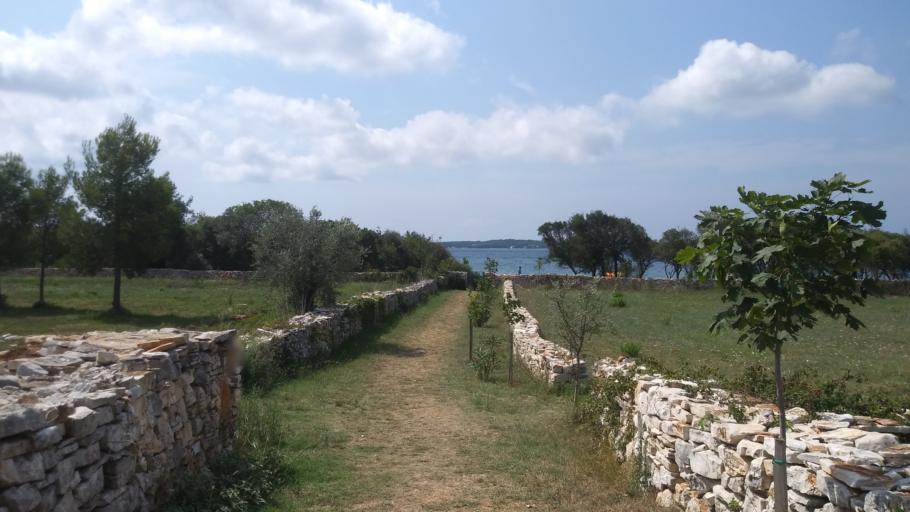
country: HR
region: Istarska
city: Fazana
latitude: 44.9482
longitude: 13.7874
